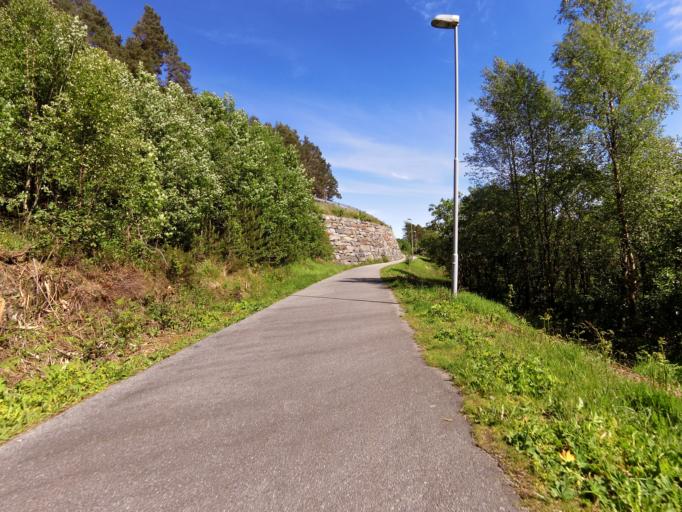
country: NO
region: Hordaland
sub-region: Stord
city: Sagvag
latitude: 59.7816
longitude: 5.3833
